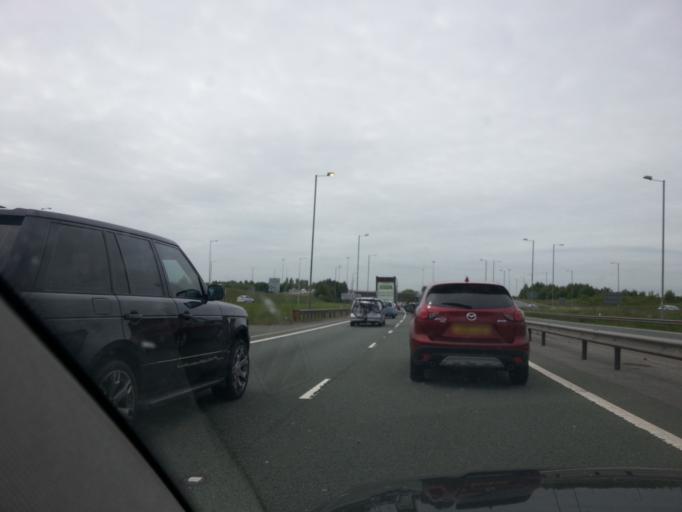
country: GB
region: England
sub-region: Cheshire West and Chester
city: Shotwick
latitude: 53.2331
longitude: -2.9911
